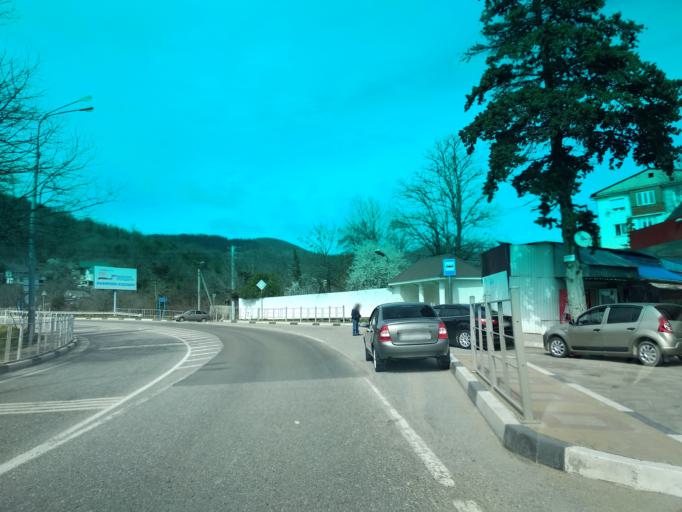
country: RU
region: Krasnodarskiy
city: Shepsi
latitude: 44.0415
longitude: 39.1509
